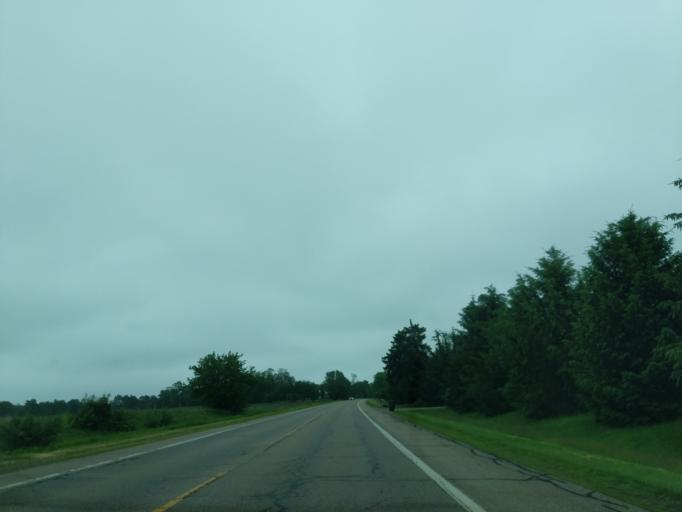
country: US
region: Michigan
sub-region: Hillsdale County
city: Jonesville
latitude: 42.0253
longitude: -84.7026
